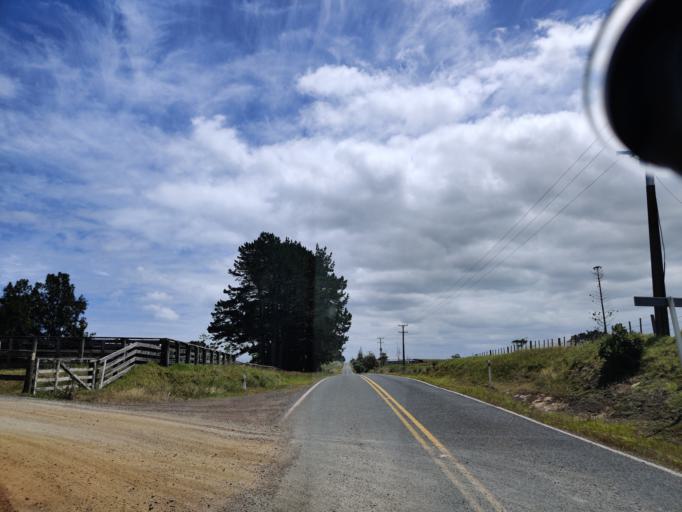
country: NZ
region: Northland
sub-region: Far North District
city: Kaitaia
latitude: -34.7060
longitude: 173.0318
